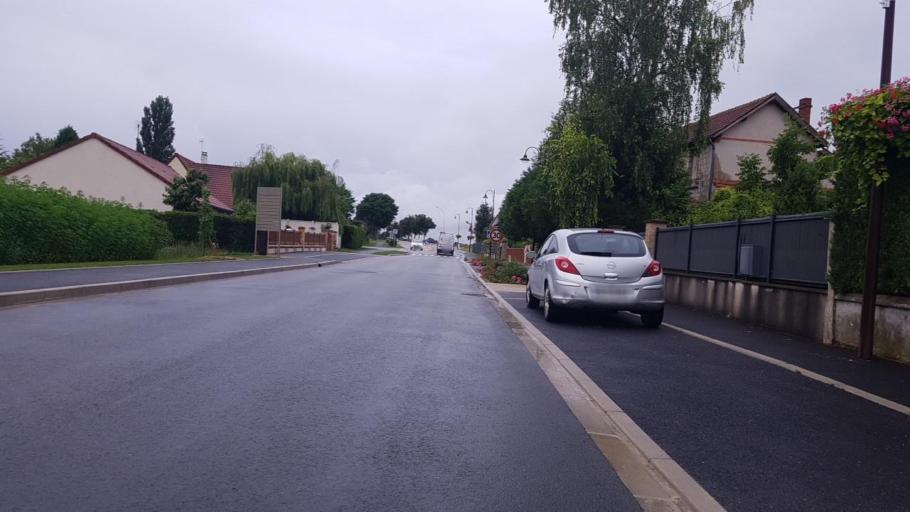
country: FR
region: Champagne-Ardenne
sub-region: Departement de la Marne
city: Sarry
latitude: 48.9219
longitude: 4.4008
